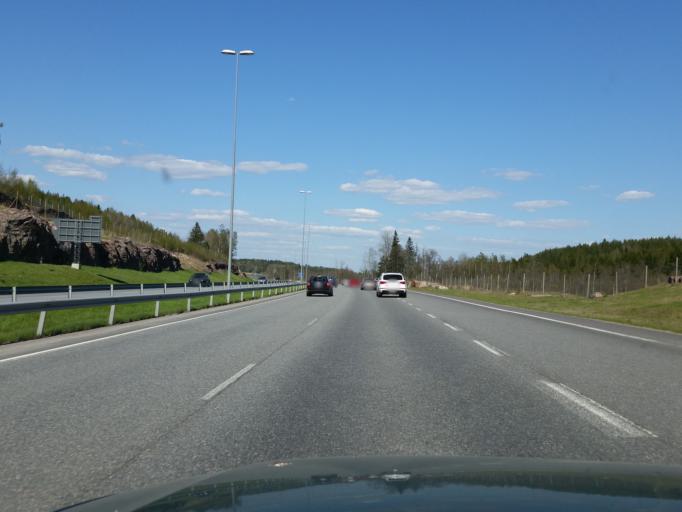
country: FI
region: Uusimaa
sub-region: Helsinki
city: Kirkkonummi
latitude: 60.1217
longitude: 24.4850
